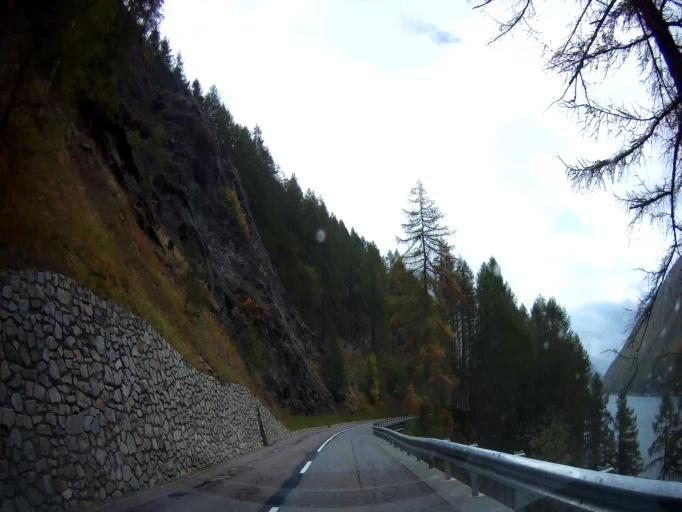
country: IT
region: Trentino-Alto Adige
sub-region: Bolzano
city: Senales
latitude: 46.7388
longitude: 10.8297
